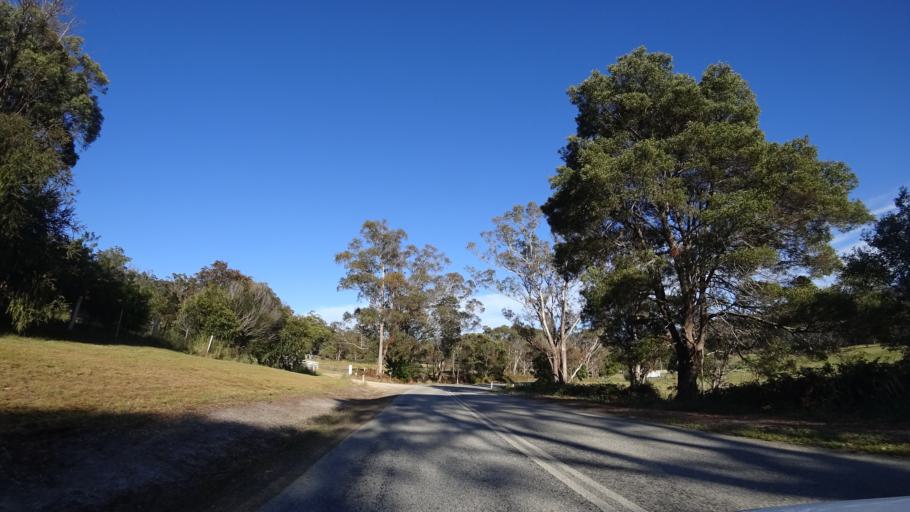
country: AU
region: Tasmania
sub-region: Break O'Day
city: St Helens
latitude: -41.2612
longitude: 148.0887
